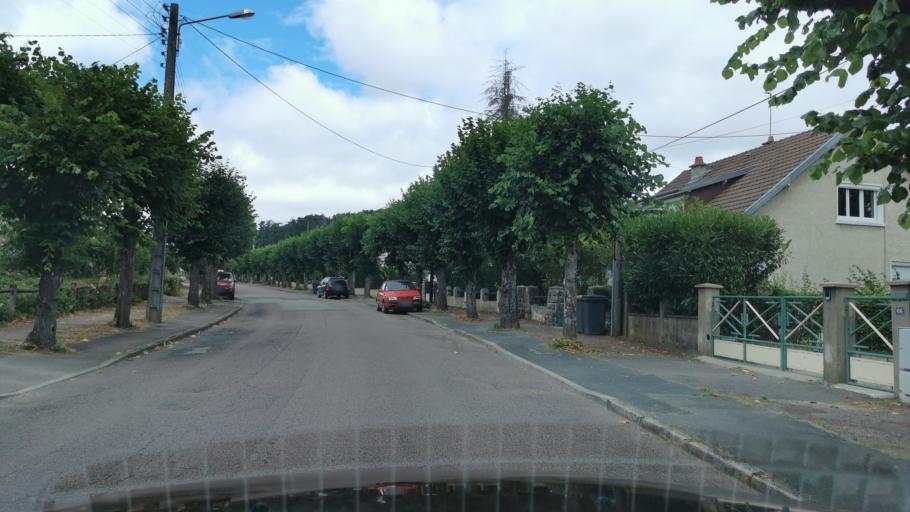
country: FR
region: Bourgogne
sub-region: Departement de Saone-et-Loire
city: Le Breuil
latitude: 46.8081
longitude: 4.4488
